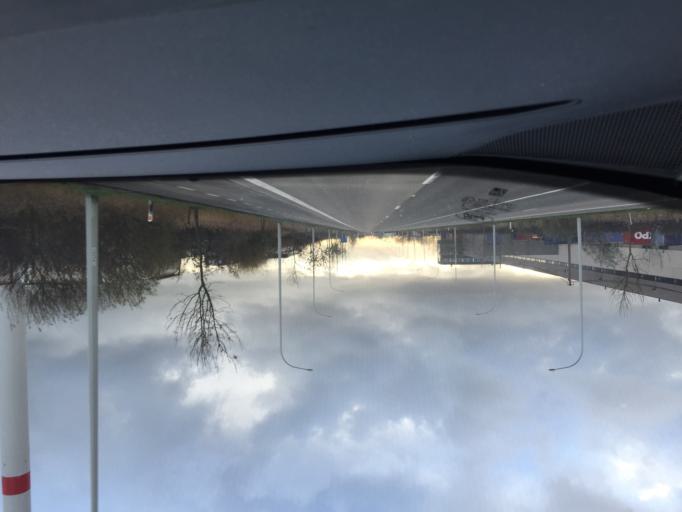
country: BE
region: Flanders
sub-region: Provincie West-Vlaanderen
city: Zeebrugge
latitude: 51.3131
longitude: 3.1873
